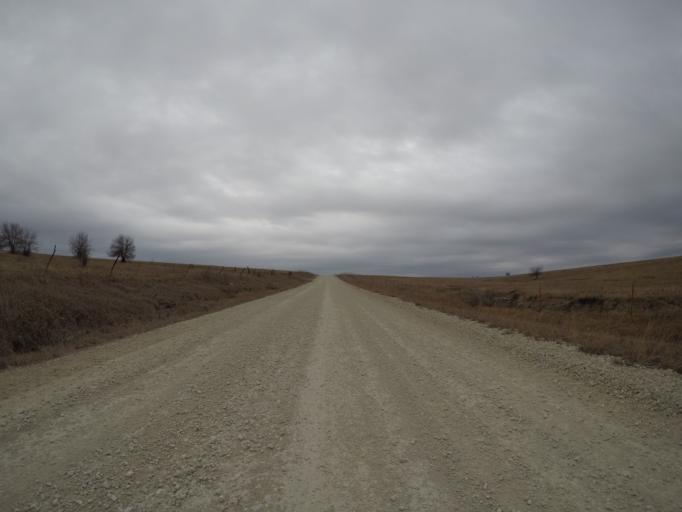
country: US
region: Kansas
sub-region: Wabaunsee County
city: Alma
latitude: 38.7905
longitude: -96.1500
